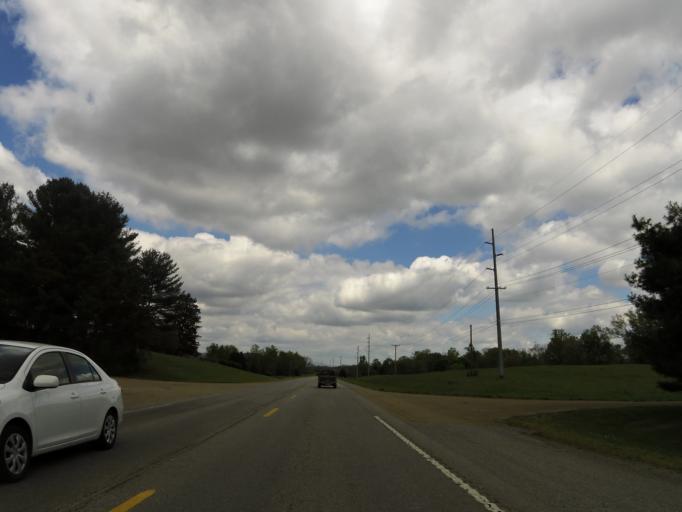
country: US
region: Kentucky
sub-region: Bell County
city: Middlesboro
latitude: 36.4909
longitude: -83.8220
